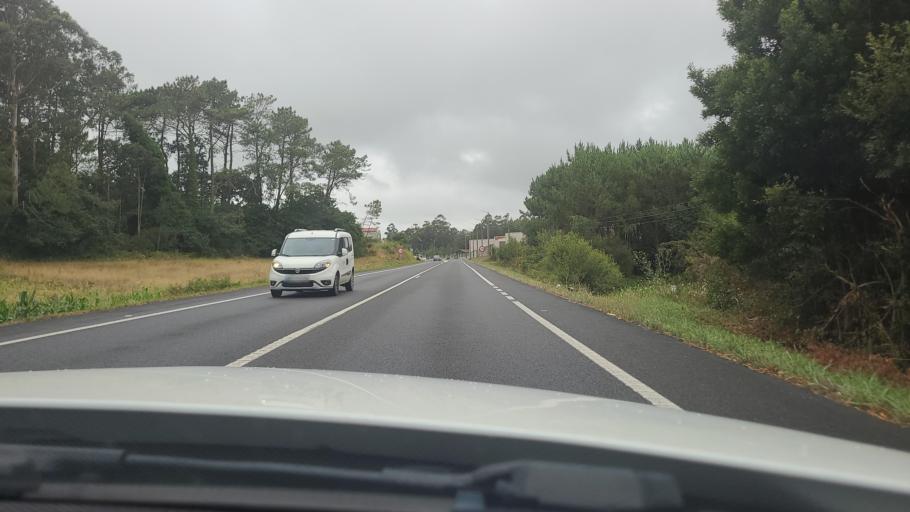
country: ES
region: Galicia
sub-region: Provincia da Coruna
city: Dumbria
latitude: 43.0097
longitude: -9.1629
